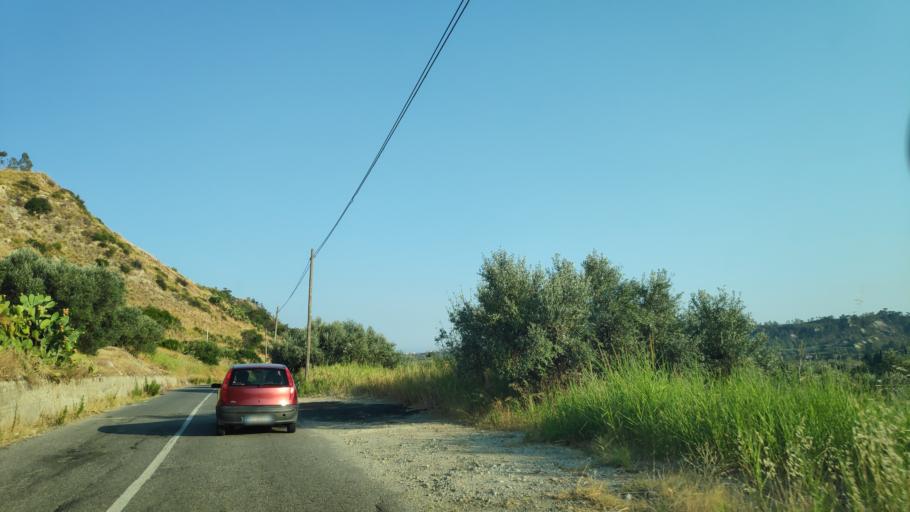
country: IT
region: Calabria
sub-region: Provincia di Reggio Calabria
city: Caulonia
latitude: 38.3790
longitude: 16.4391
